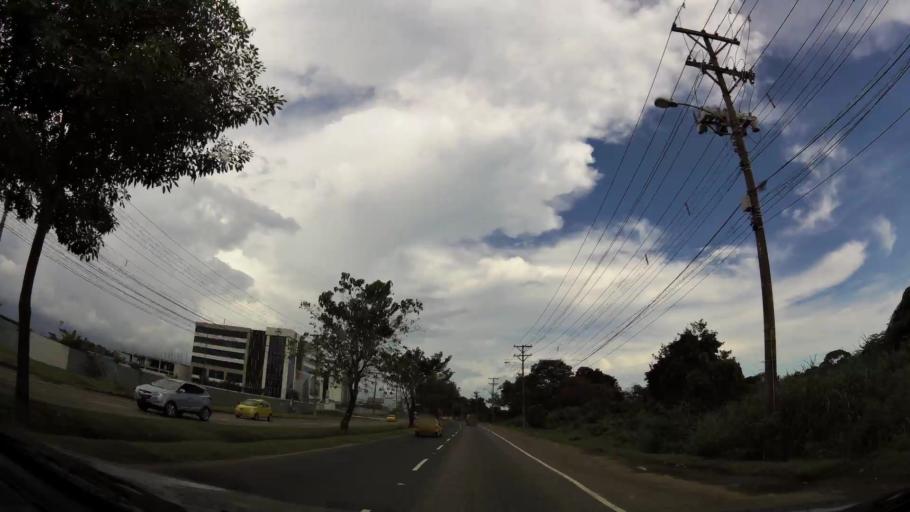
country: PA
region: Panama
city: Tocumen
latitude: 9.0693
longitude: -79.3963
